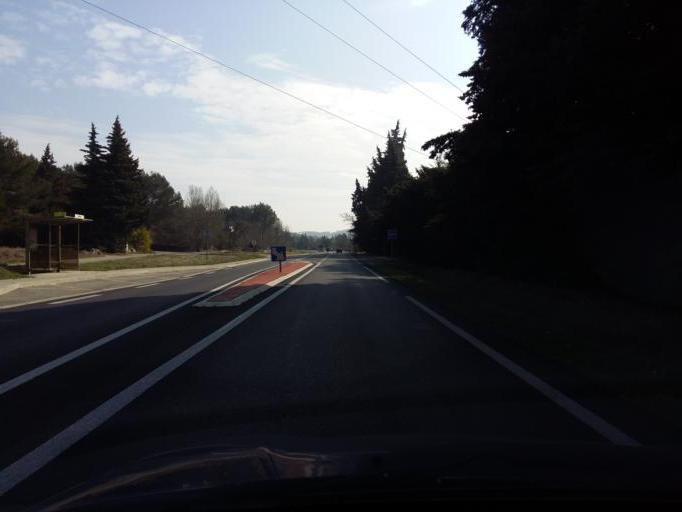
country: FR
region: Provence-Alpes-Cote d'Azur
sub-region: Departement des Bouches-du-Rhone
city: Orgon
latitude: 43.7977
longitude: 5.0104
